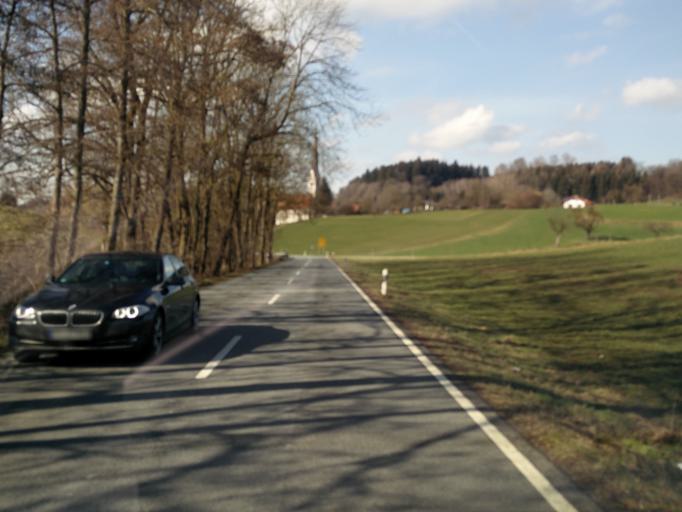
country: DE
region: Bavaria
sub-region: Upper Bavaria
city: Rimsting
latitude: 47.8913
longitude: 12.3217
